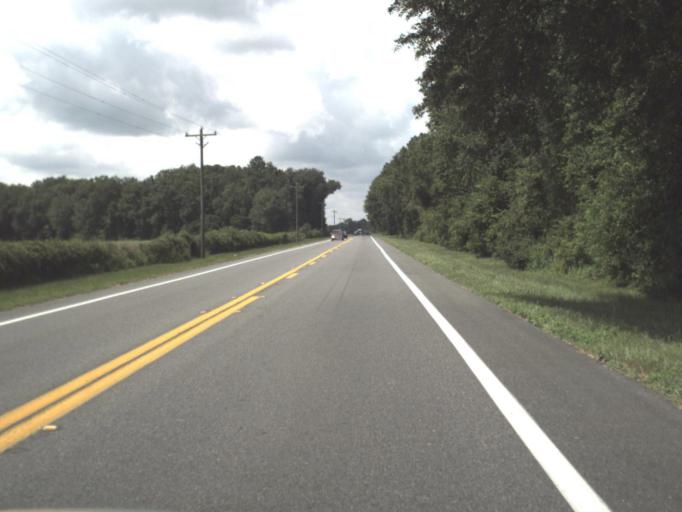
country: US
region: Florida
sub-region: Union County
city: Lake Butler
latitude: 29.9607
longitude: -82.4102
